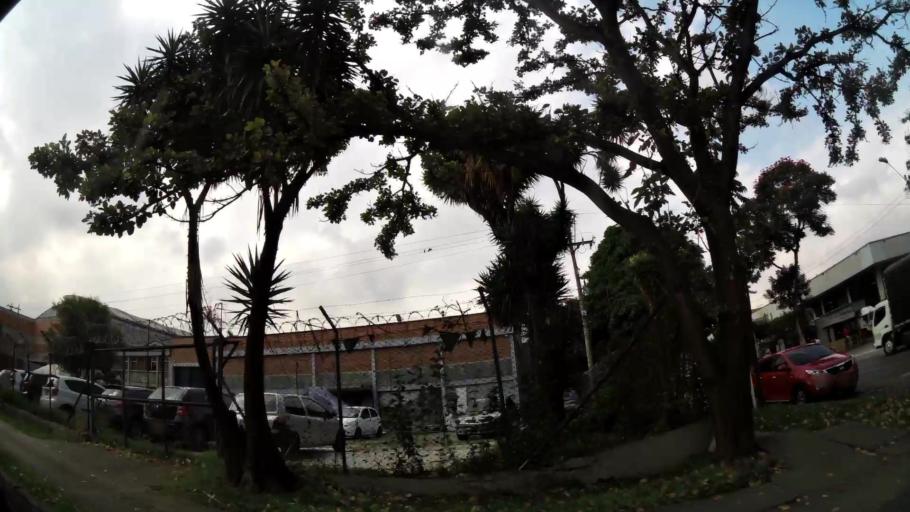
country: CO
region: Antioquia
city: Itagui
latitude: 6.2184
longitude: -75.5842
